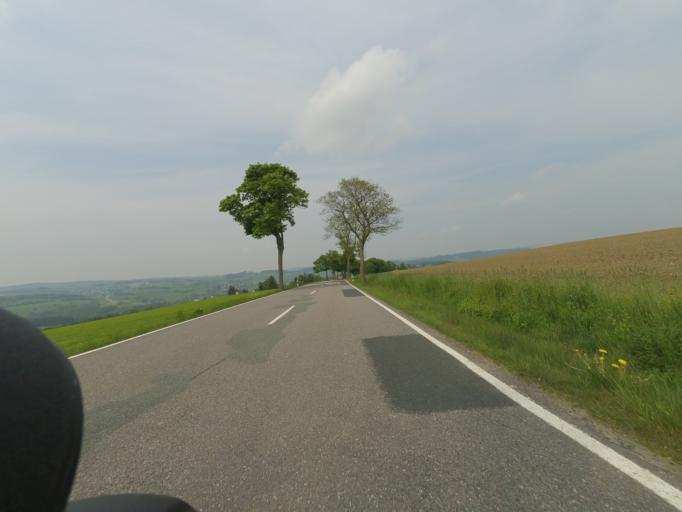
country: DE
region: Saxony
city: Wolkenstein
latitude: 50.6492
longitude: 13.0863
